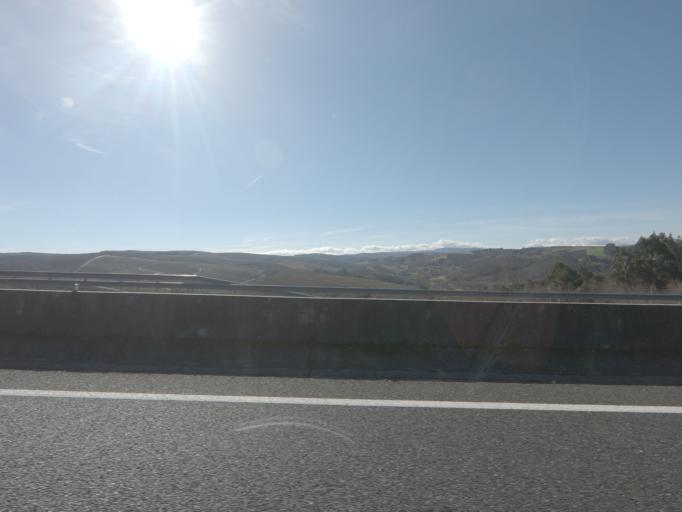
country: ES
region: Galicia
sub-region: Provincia de Pontevedra
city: Dozon
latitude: 42.5849
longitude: -8.0718
